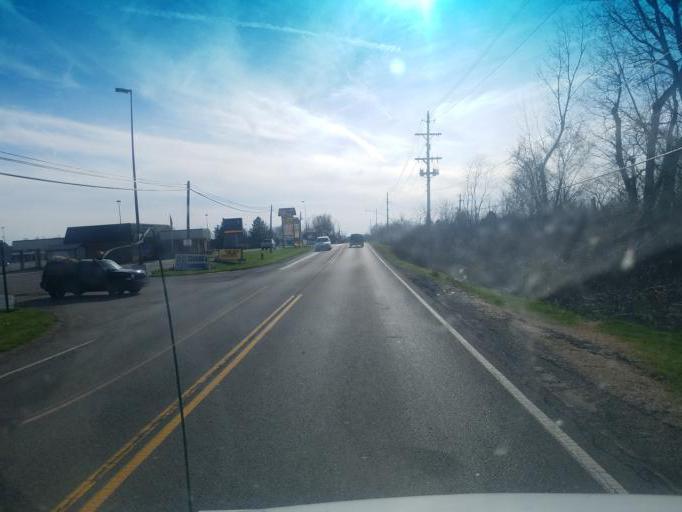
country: US
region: Ohio
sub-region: Logan County
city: Bellefontaine
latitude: 40.3663
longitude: -83.7369
